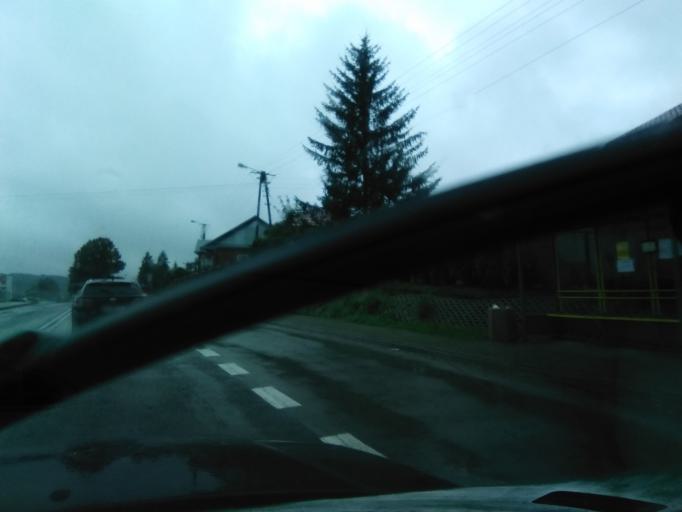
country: PL
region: Subcarpathian Voivodeship
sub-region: Powiat ropczycko-sedziszowski
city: Niedzwiada
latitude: 49.9977
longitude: 21.5629
